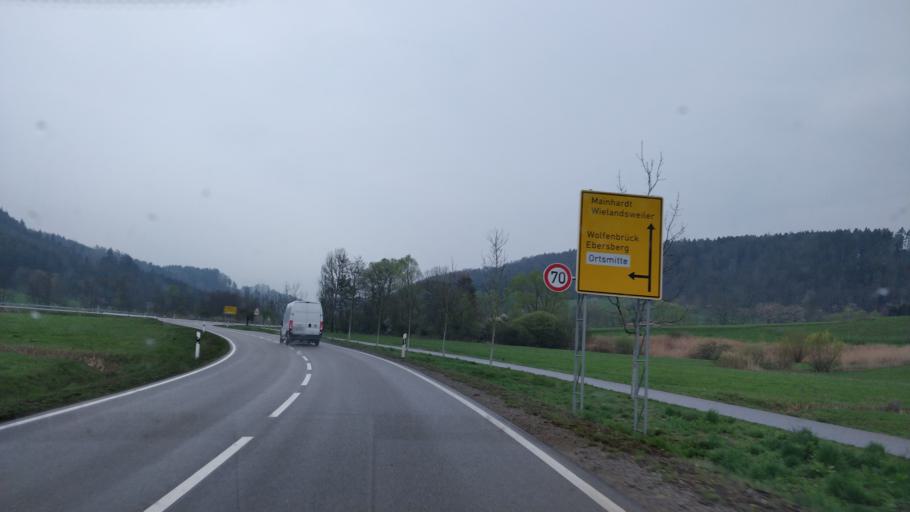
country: DE
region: Baden-Wuerttemberg
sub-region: Regierungsbezirk Stuttgart
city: Oberrot
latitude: 49.0194
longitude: 9.6631
